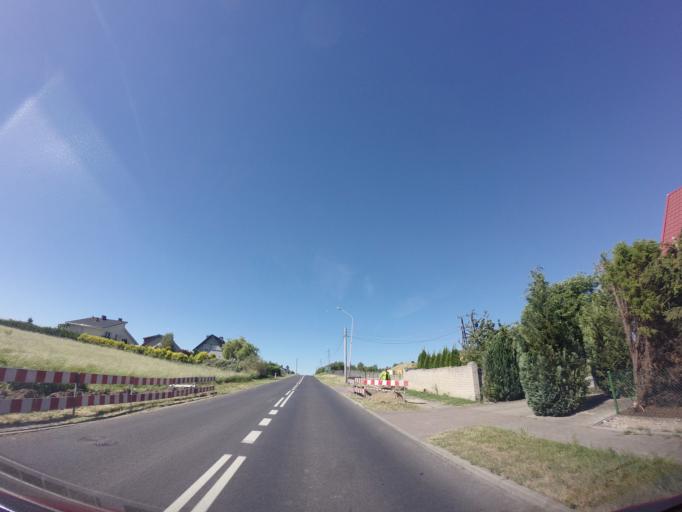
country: PL
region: West Pomeranian Voivodeship
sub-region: Powiat stargardzki
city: Dolice
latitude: 53.1860
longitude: 15.1963
